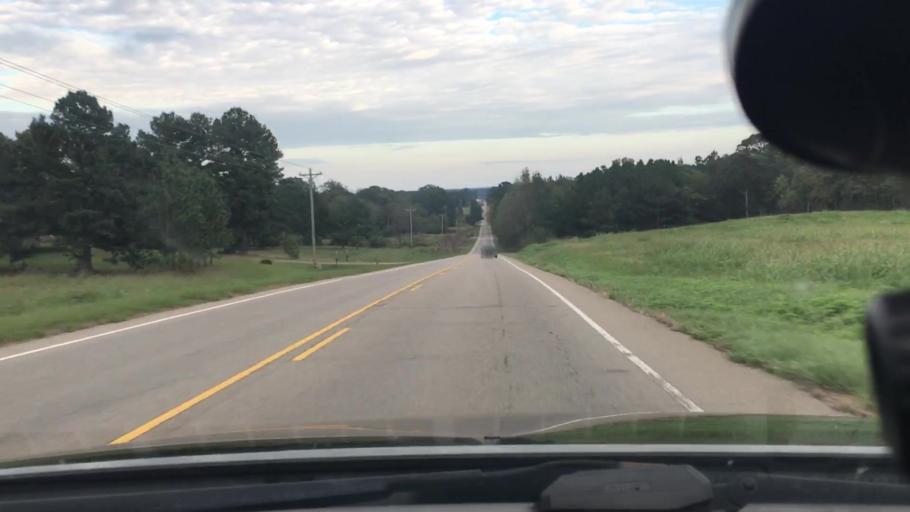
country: US
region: North Carolina
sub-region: Moore County
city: Robbins
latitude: 35.3915
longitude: -79.5174
